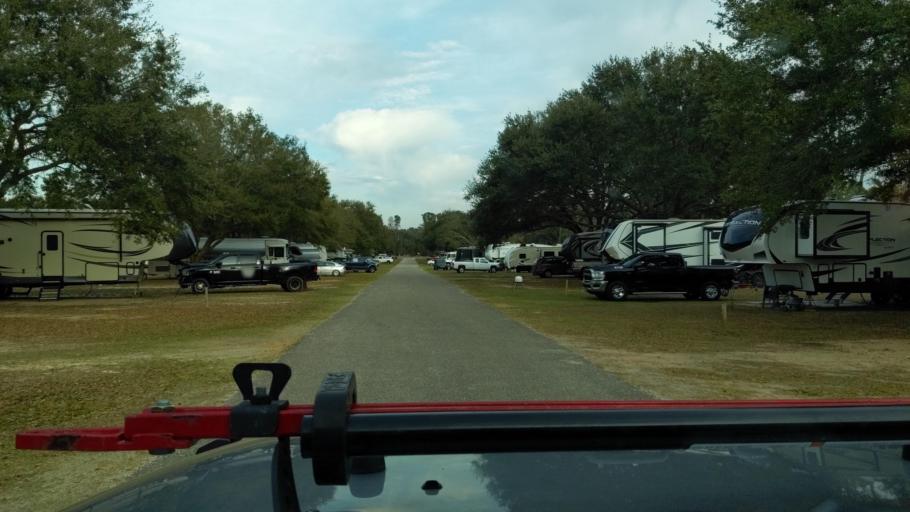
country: US
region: Alabama
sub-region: Baldwin County
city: Foley
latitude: 30.4584
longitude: -87.7824
